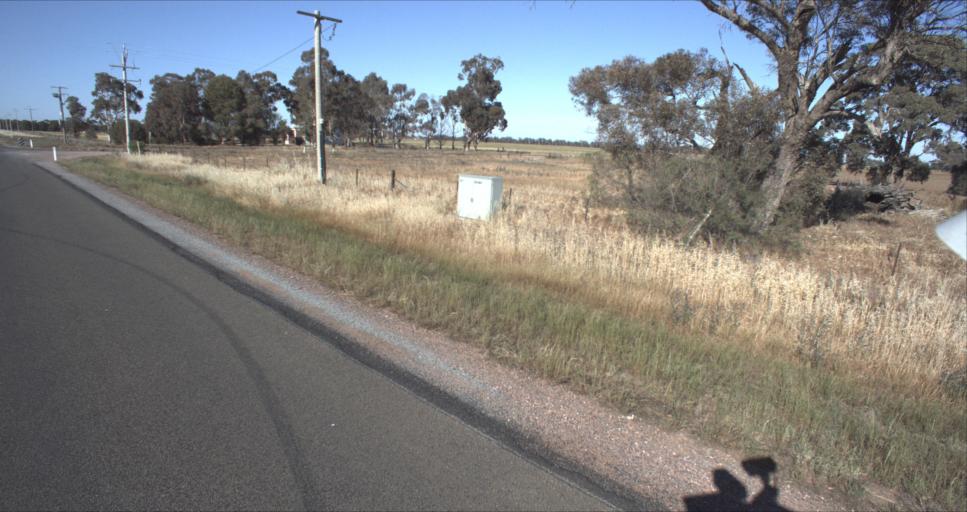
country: AU
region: New South Wales
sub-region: Leeton
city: Leeton
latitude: -34.5769
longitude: 146.2624
